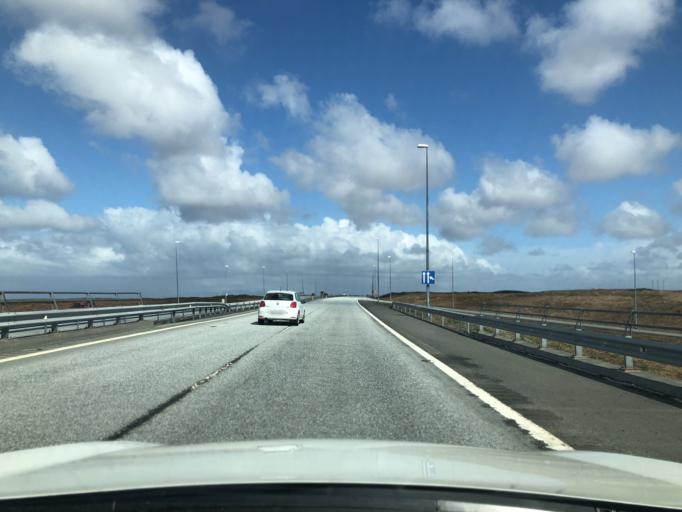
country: IS
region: Southern Peninsula
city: Vogar
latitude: 63.9740
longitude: -22.3585
